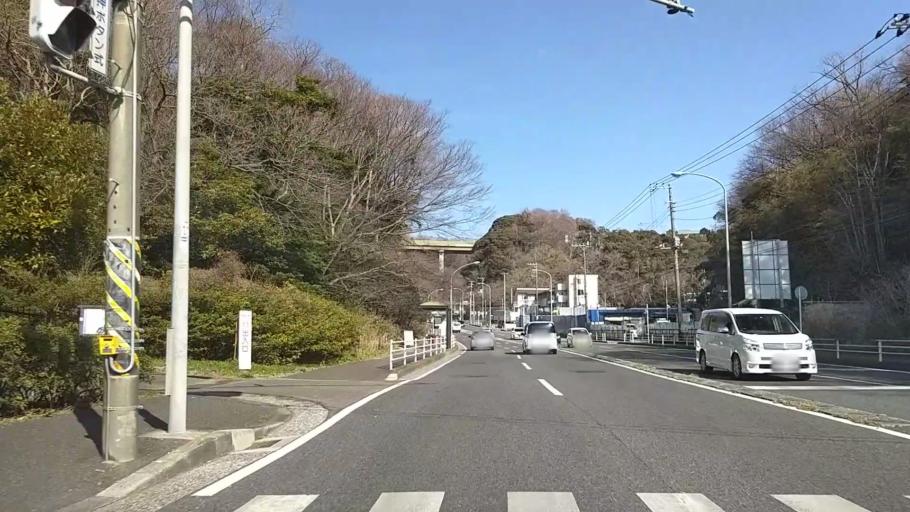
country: JP
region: Kanagawa
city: Zushi
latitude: 35.3515
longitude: 139.6069
